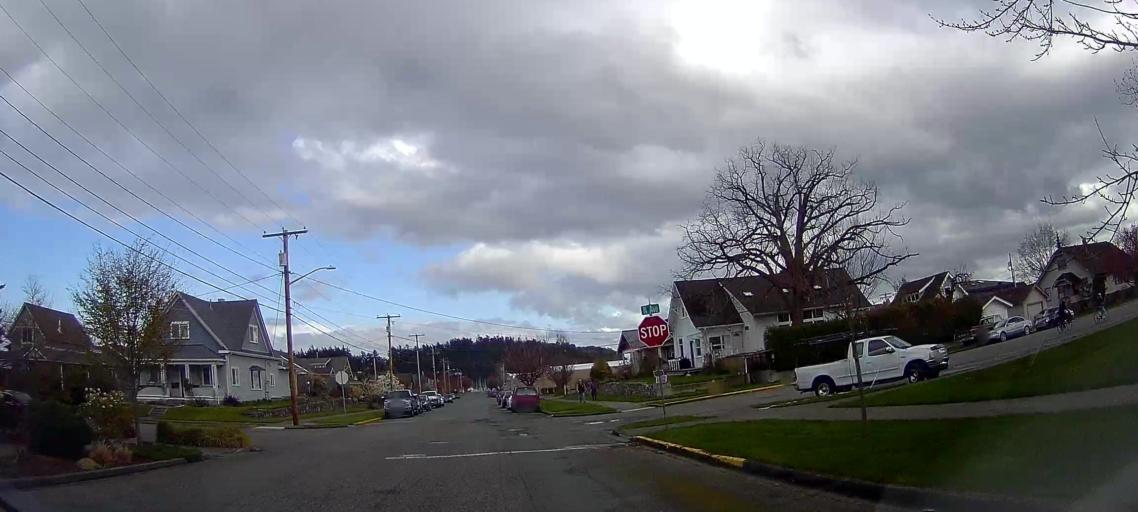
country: US
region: Washington
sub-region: Skagit County
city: Anacortes
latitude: 48.5151
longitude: -122.6163
